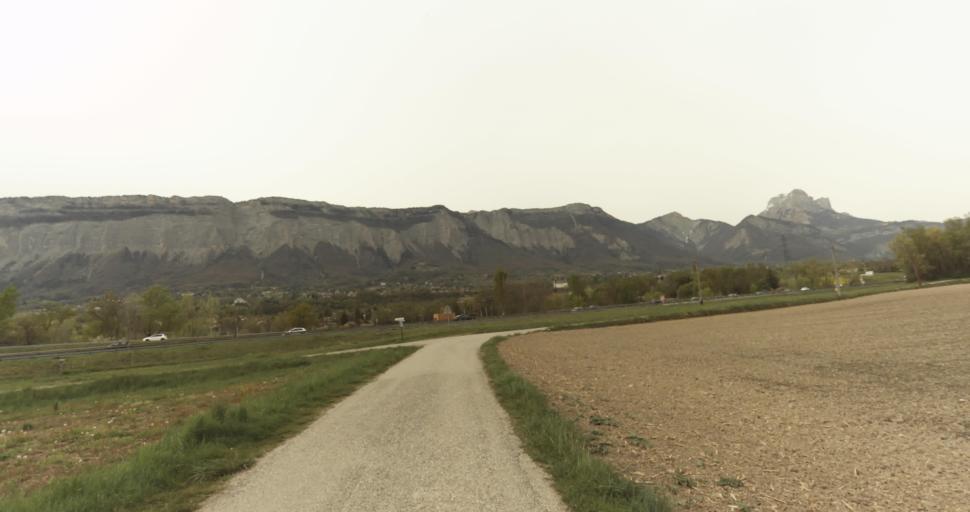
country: FR
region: Rhone-Alpes
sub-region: Departement de l'Isere
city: Montbonnot-Saint-Martin
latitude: 45.2241
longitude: 5.8244
